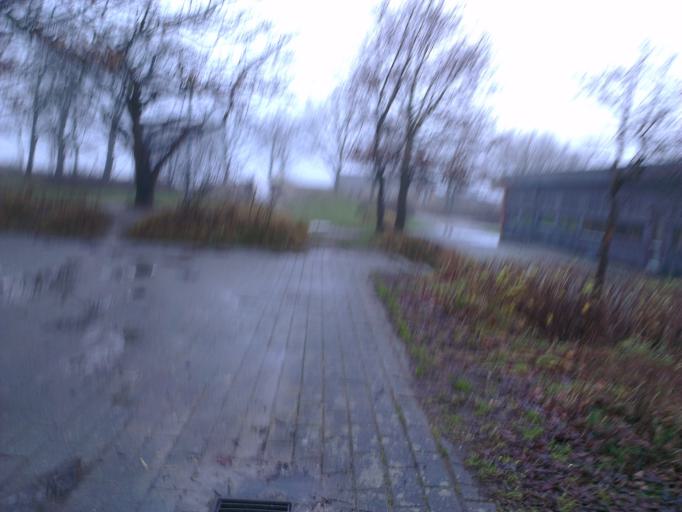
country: DK
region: Capital Region
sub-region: Frederikssund Kommune
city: Jaegerspris
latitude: 55.8454
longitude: 11.9858
